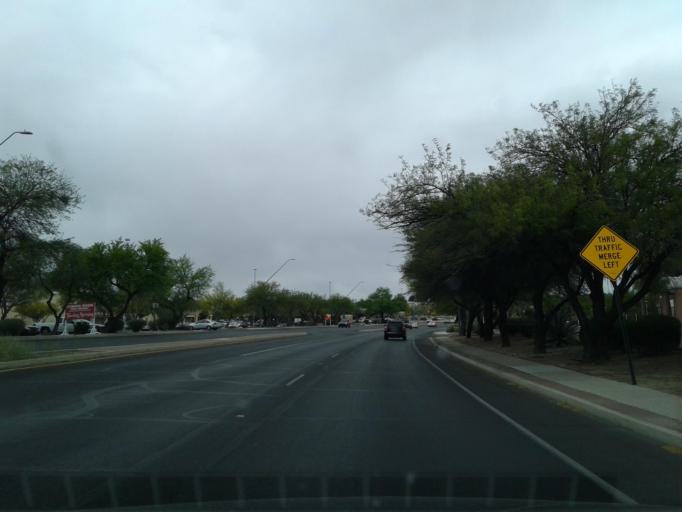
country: US
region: Arizona
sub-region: Pima County
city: Casas Adobes
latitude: 32.2936
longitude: -110.9709
